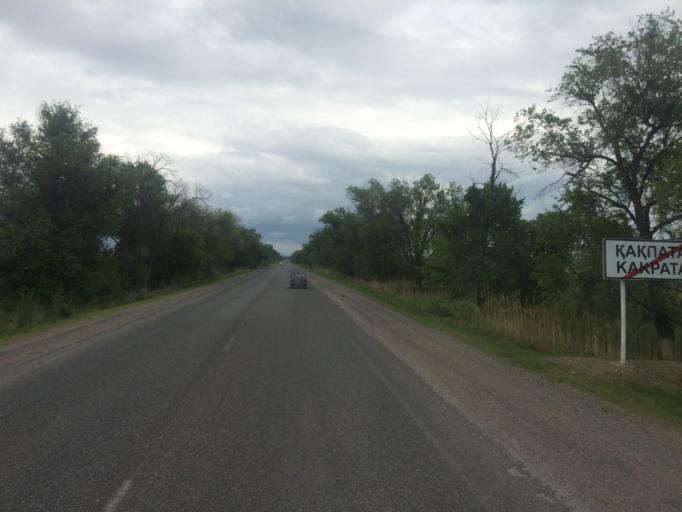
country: KZ
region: Zhambyl
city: Georgiyevka
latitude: 43.2261
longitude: 74.4071
